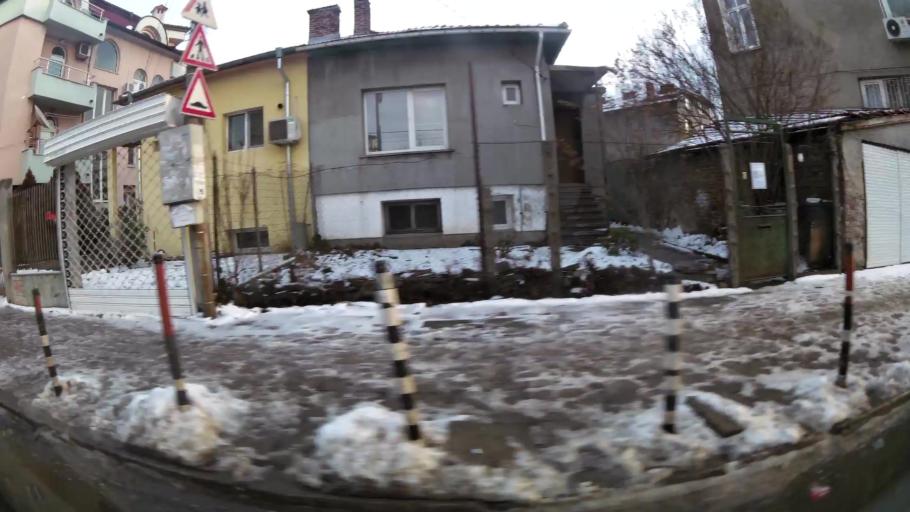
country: BG
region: Sofia-Capital
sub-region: Stolichna Obshtina
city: Sofia
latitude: 42.7171
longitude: 23.3425
